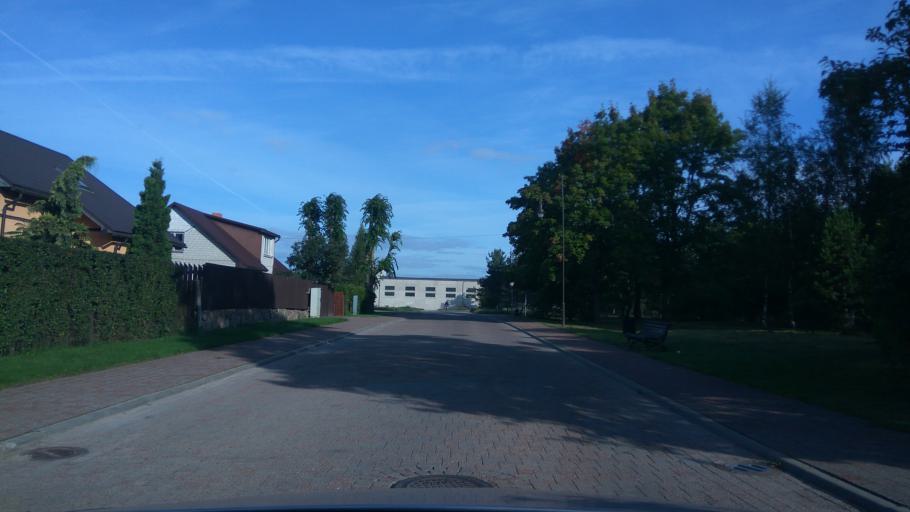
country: LV
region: Kuldigas Rajons
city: Kuldiga
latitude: 56.9748
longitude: 21.9691
